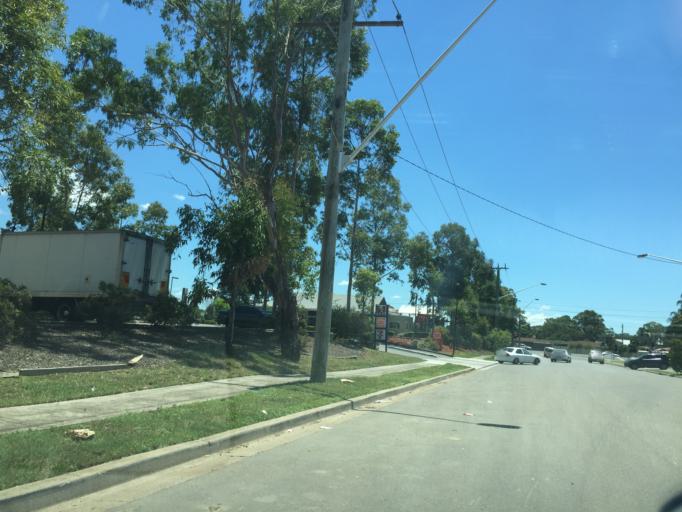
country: AU
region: New South Wales
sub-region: Blacktown
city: Mount Druitt
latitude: -33.7795
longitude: 150.8088
